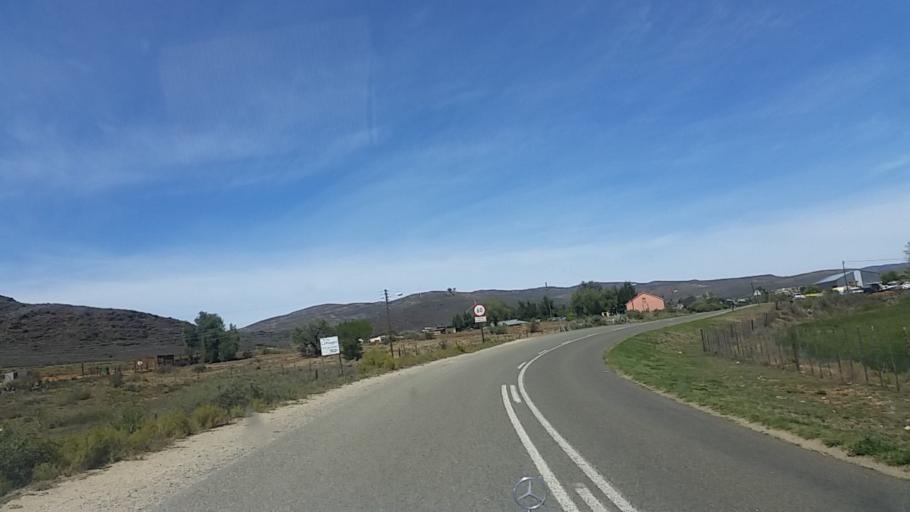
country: ZA
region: Western Cape
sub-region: Eden District Municipality
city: Knysna
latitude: -33.6436
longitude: 23.1382
